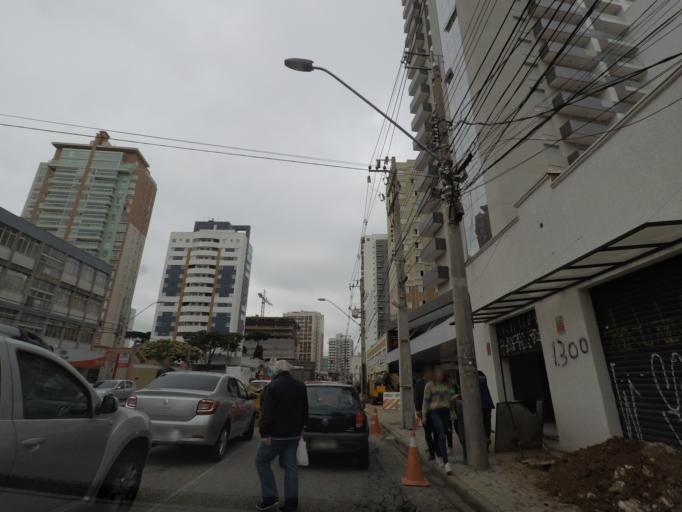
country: BR
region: Parana
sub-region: Curitiba
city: Curitiba
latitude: -25.4580
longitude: -49.2889
